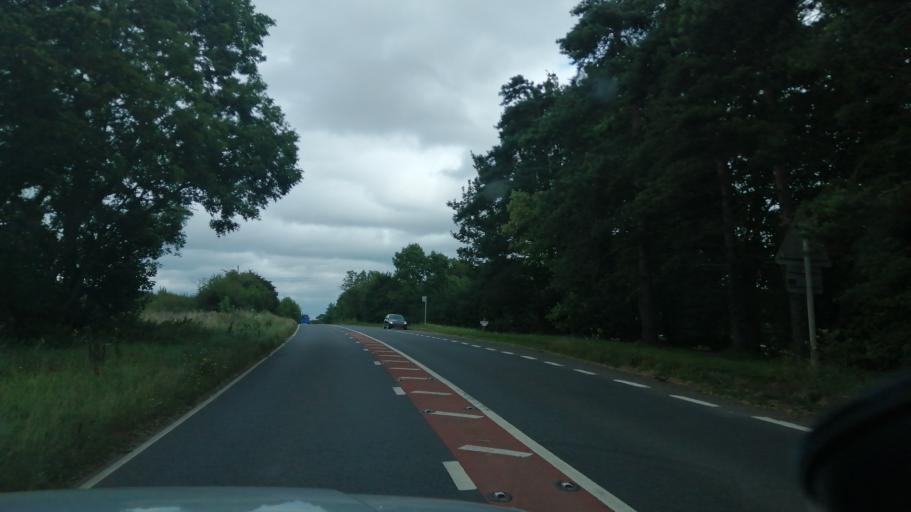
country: GB
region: England
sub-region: Herefordshire
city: Thruxton
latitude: 51.9852
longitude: -2.8017
